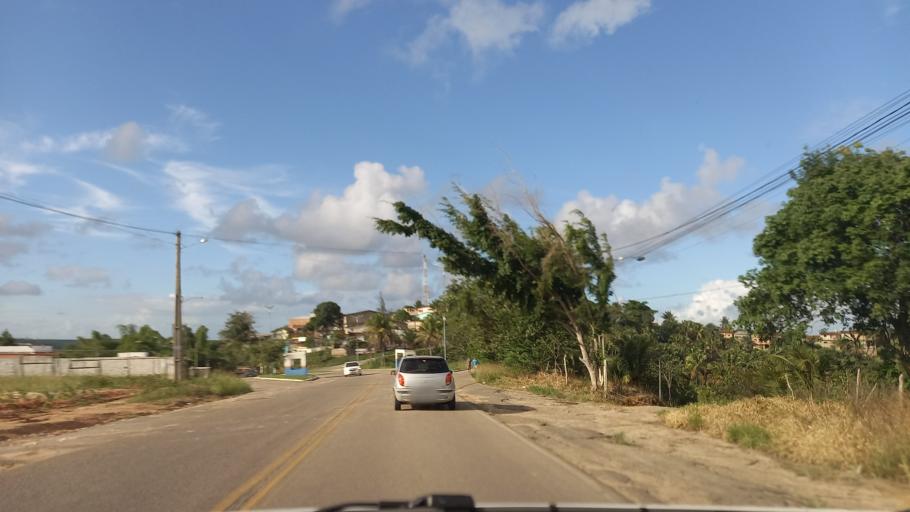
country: BR
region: Pernambuco
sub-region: Rio Formoso
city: Rio Formoso
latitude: -8.6729
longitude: -35.1584
